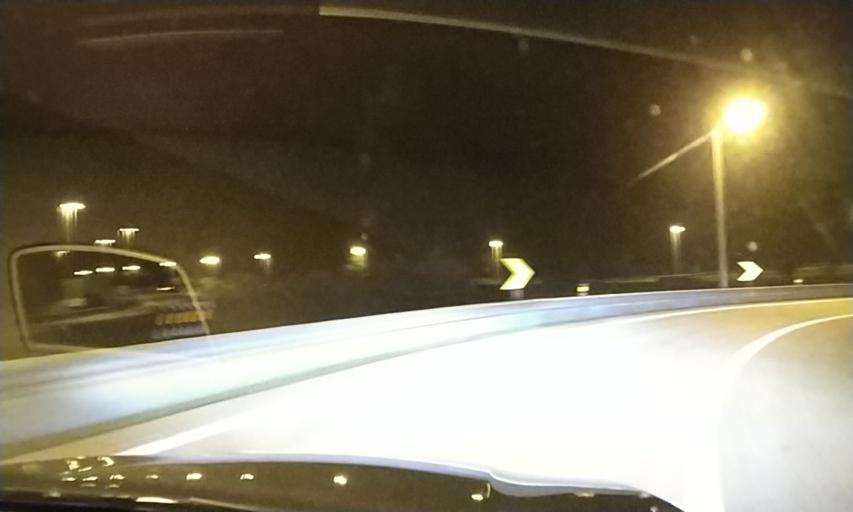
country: PT
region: Setubal
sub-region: Montijo
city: Montijo
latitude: 38.7186
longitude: -8.9428
